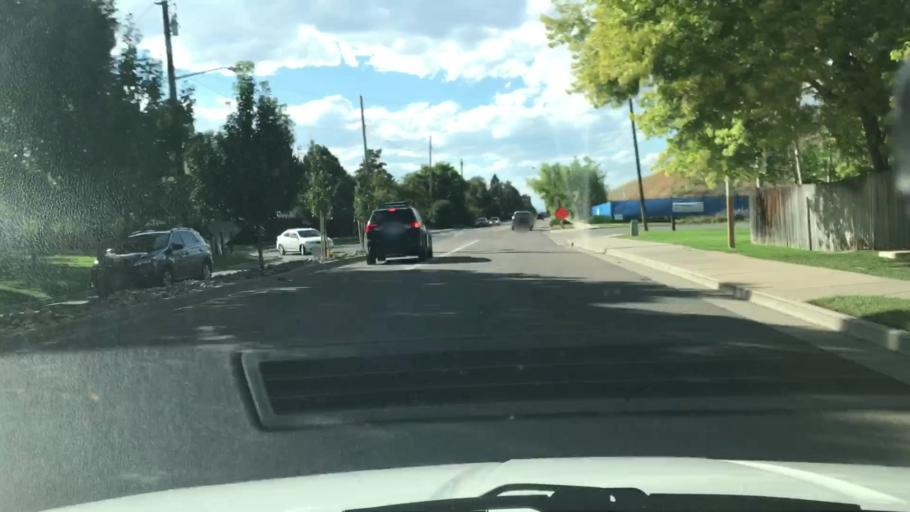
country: US
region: Colorado
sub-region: Arapahoe County
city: Greenwood Village
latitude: 39.6386
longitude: -104.9131
